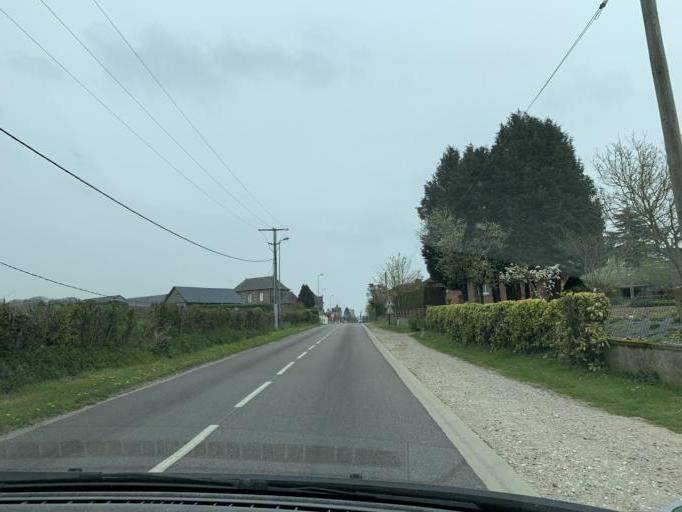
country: FR
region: Haute-Normandie
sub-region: Departement de la Seine-Maritime
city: Londinieres
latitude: 49.8428
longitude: 1.4737
